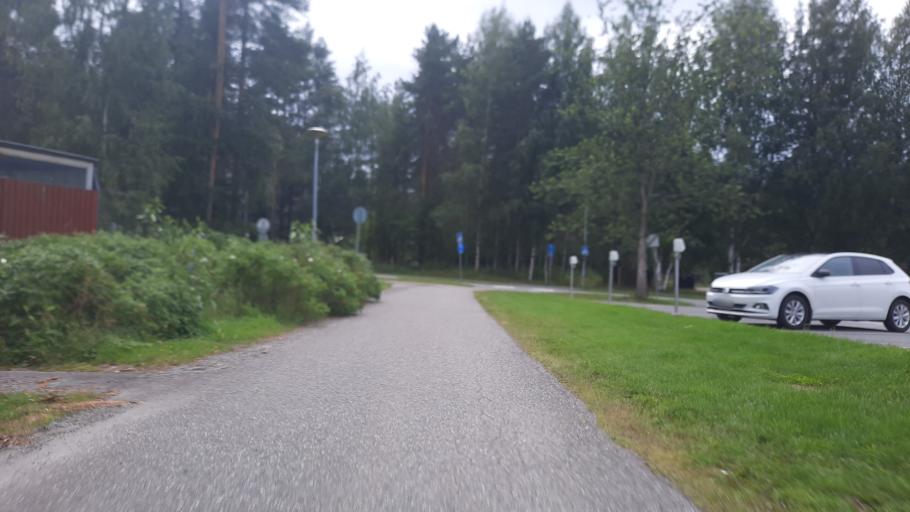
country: FI
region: North Karelia
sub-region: Joensuu
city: Joensuu
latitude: 62.6140
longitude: 29.8147
